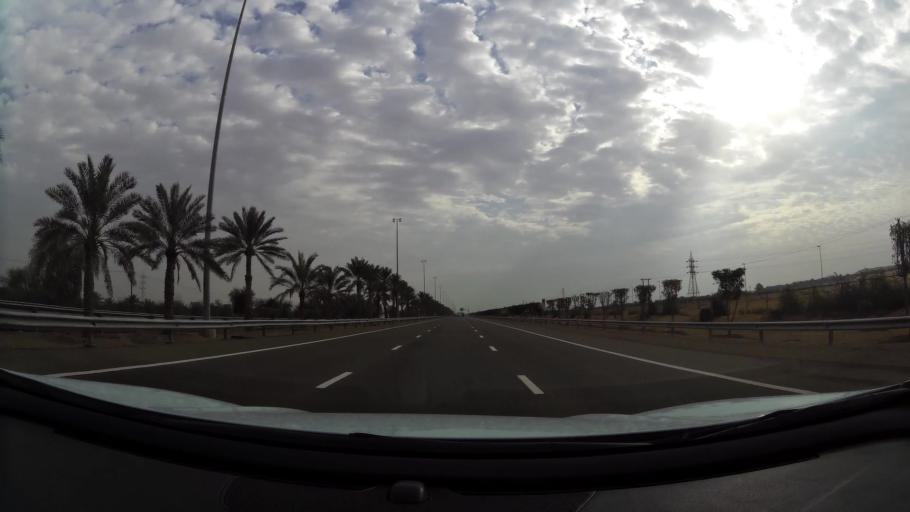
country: AE
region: Abu Dhabi
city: Al Ain
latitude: 24.2005
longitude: 55.3719
